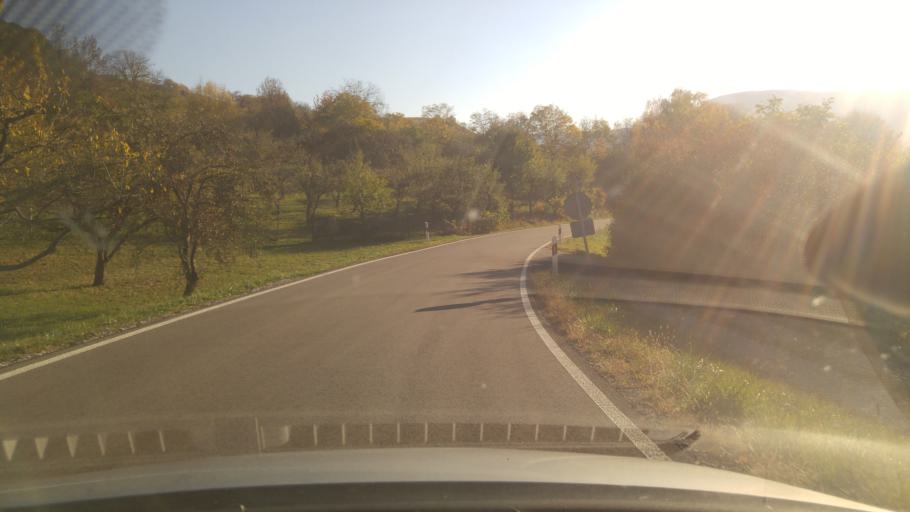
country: DE
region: Baden-Wuerttemberg
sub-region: Regierungsbezirk Stuttgart
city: Owen
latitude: 48.5916
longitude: 9.4622
